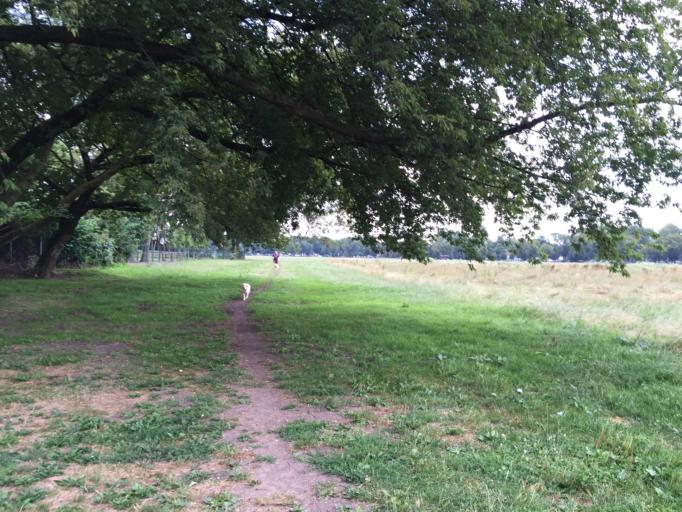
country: PL
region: Lesser Poland Voivodeship
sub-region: Krakow
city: Krakow
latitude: 50.0587
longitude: 19.9083
